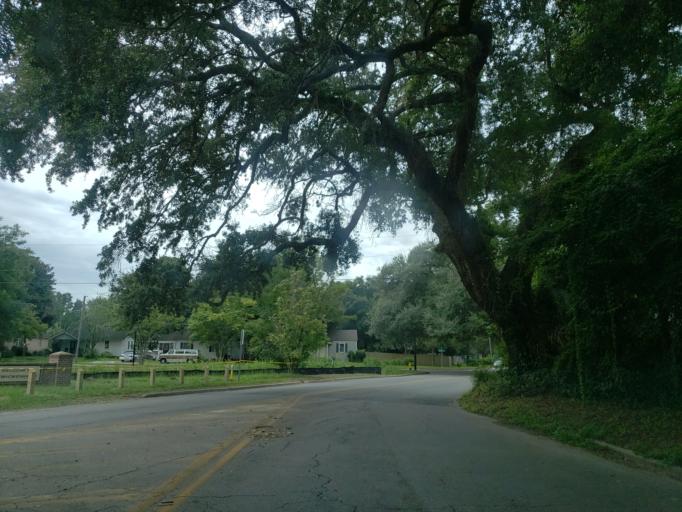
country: US
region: Georgia
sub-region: Chatham County
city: Thunderbolt
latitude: 32.0695
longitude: -81.0596
